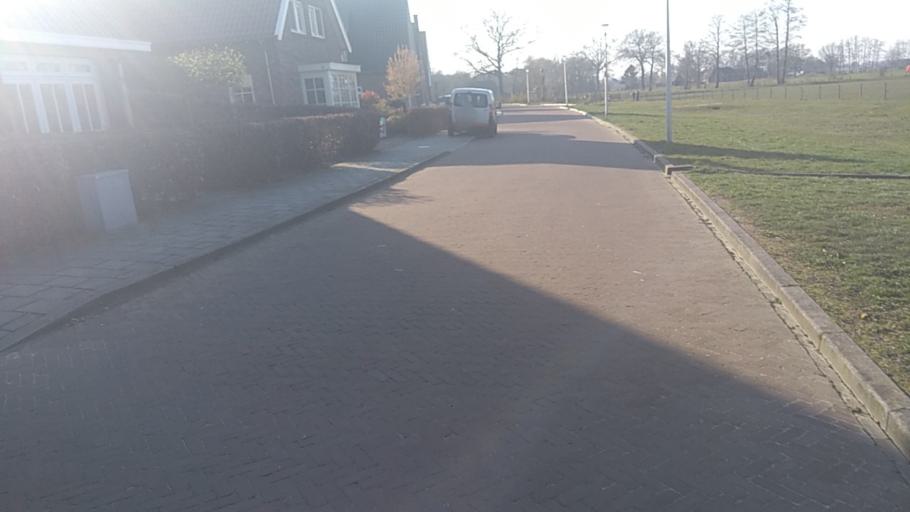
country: NL
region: Overijssel
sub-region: Gemeente Almelo
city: Almelo
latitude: 52.3852
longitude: 6.7119
